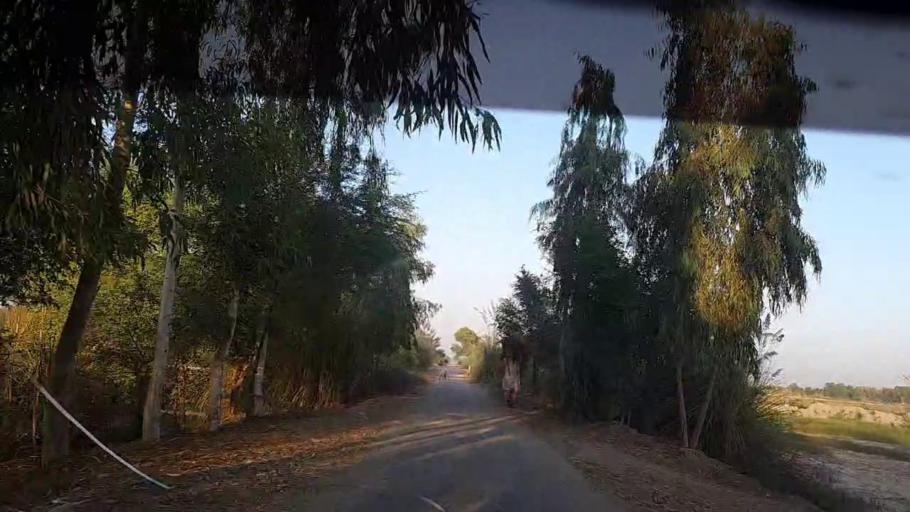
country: PK
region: Sindh
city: Ratodero
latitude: 27.8827
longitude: 68.2087
